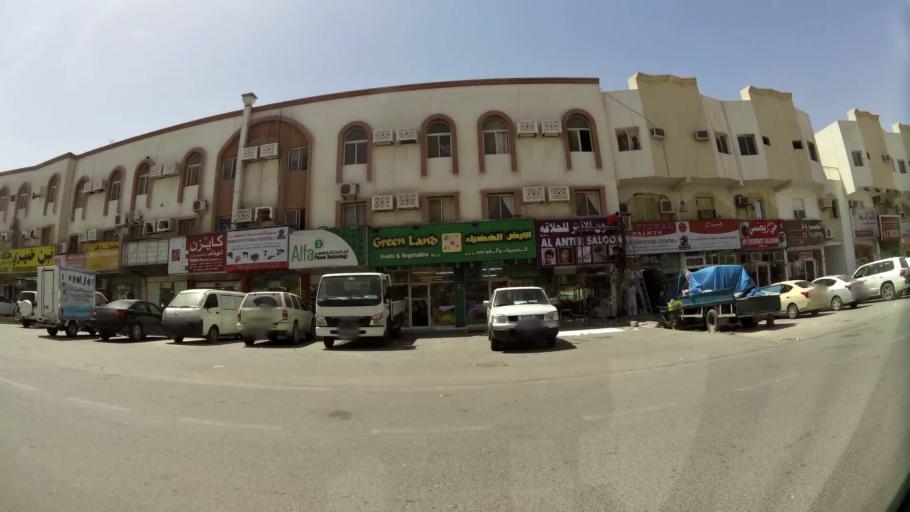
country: QA
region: Baladiyat ar Rayyan
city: Ar Rayyan
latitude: 25.2731
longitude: 51.4078
